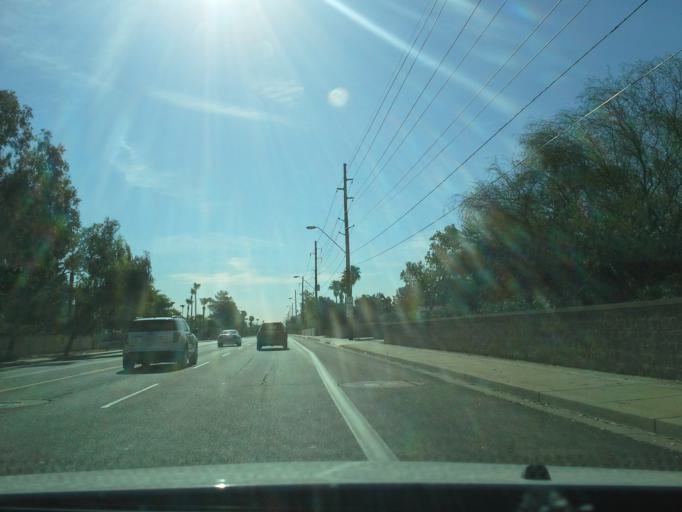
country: US
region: Arizona
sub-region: Maricopa County
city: Paradise Valley
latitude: 33.5971
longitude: -111.9599
